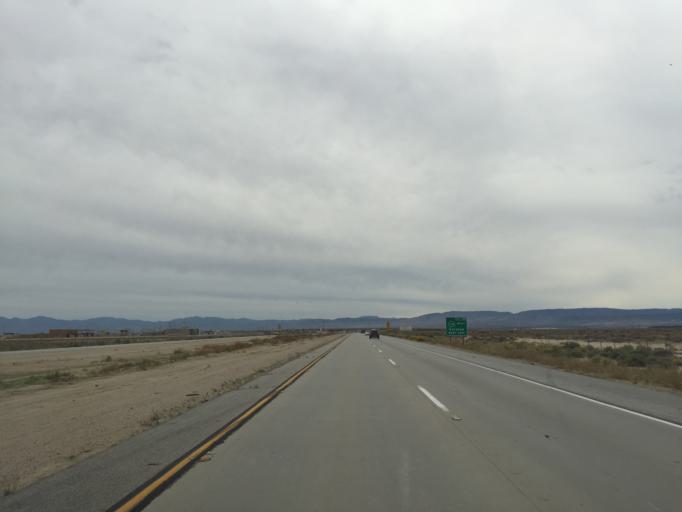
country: US
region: California
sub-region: Kern County
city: Rosamond
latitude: 34.7867
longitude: -118.1710
